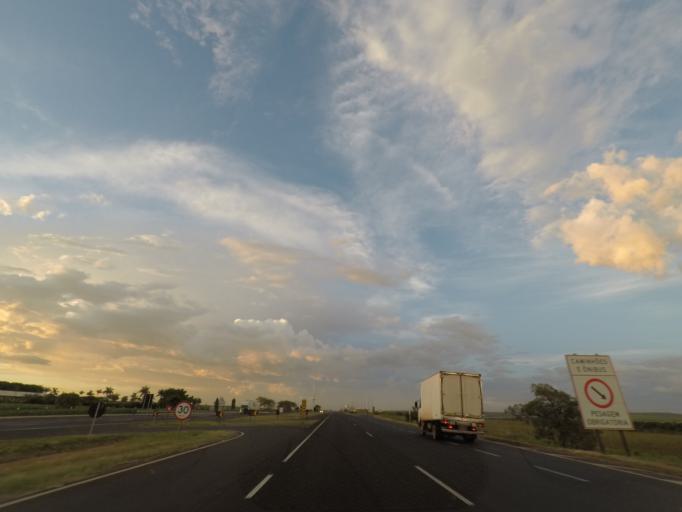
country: BR
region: Minas Gerais
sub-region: Uberaba
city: Uberaba
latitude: -19.6705
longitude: -47.9983
